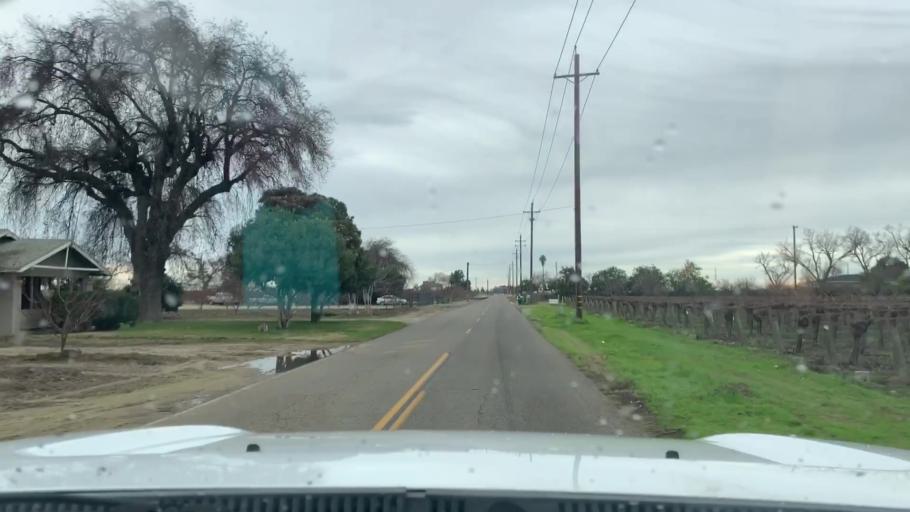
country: US
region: California
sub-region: Fresno County
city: Selma
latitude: 36.5534
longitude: -119.5751
